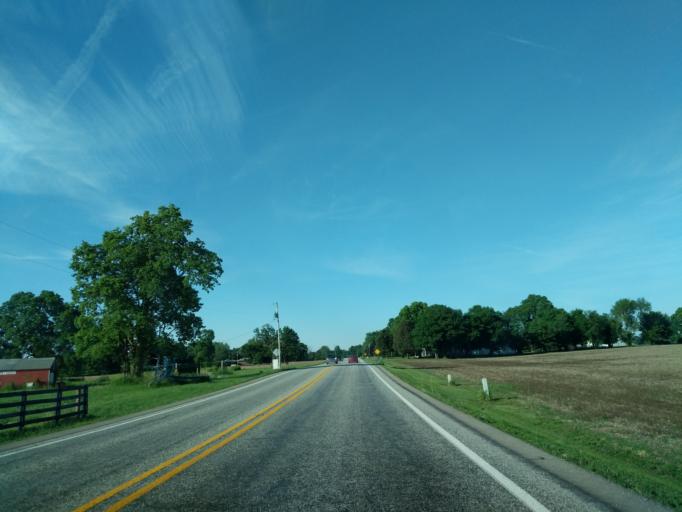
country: US
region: Indiana
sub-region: Madison County
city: Pendleton
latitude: 39.9608
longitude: -85.7592
